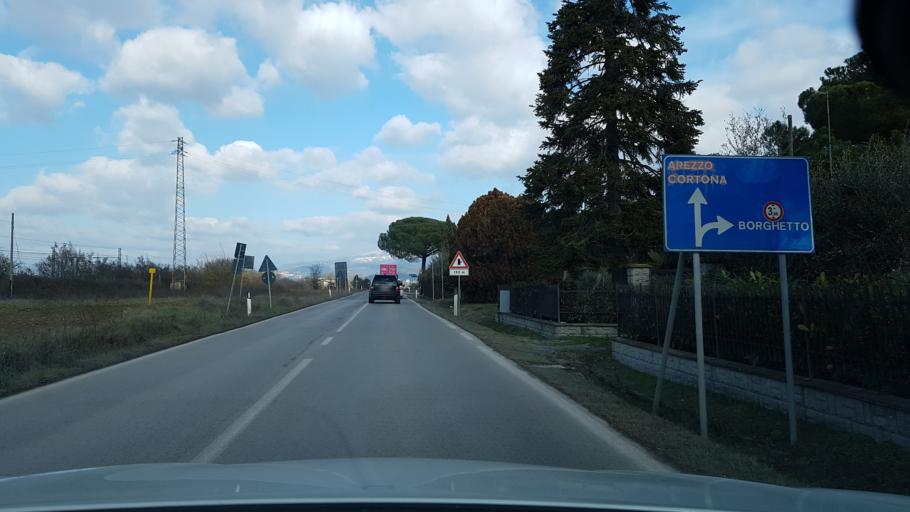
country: IT
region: Tuscany
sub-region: Province of Arezzo
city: Terontola
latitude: 43.1795
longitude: 12.0137
